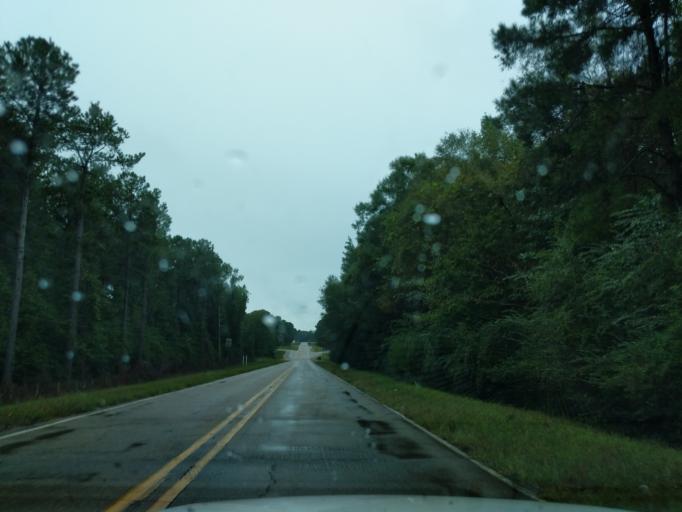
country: US
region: Louisiana
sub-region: Bienville Parish
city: Arcadia
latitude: 32.5580
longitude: -93.0541
